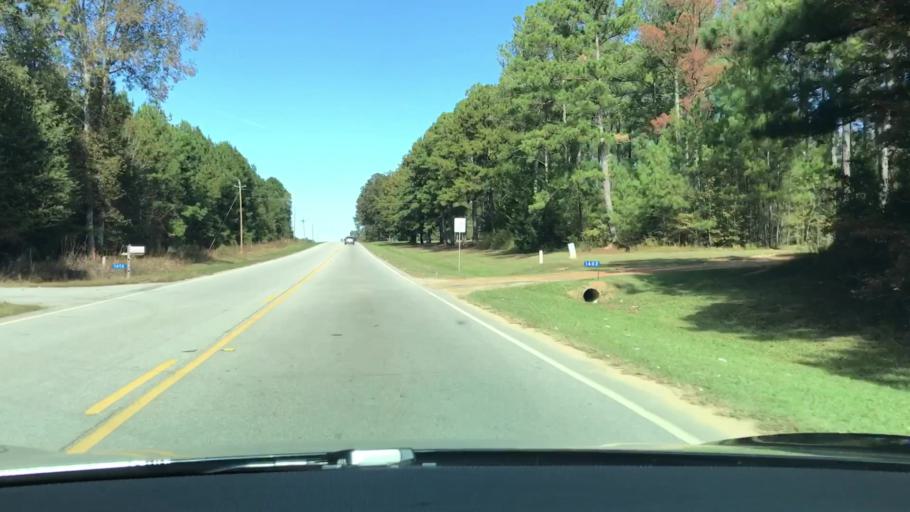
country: US
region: Georgia
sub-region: Warren County
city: West Warrenton
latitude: 33.4215
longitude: -82.6805
